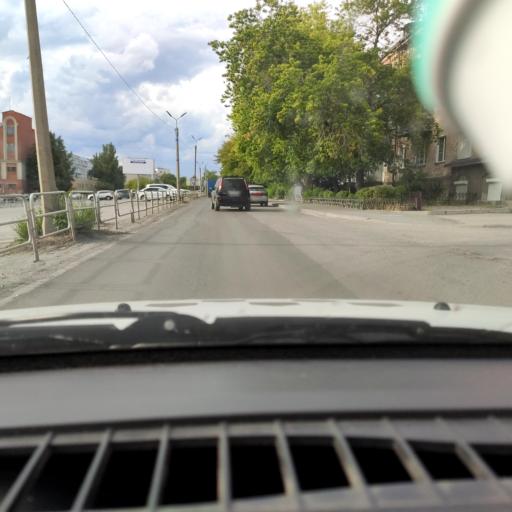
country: RU
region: Chelyabinsk
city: Miass
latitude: 55.0462
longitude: 60.1119
